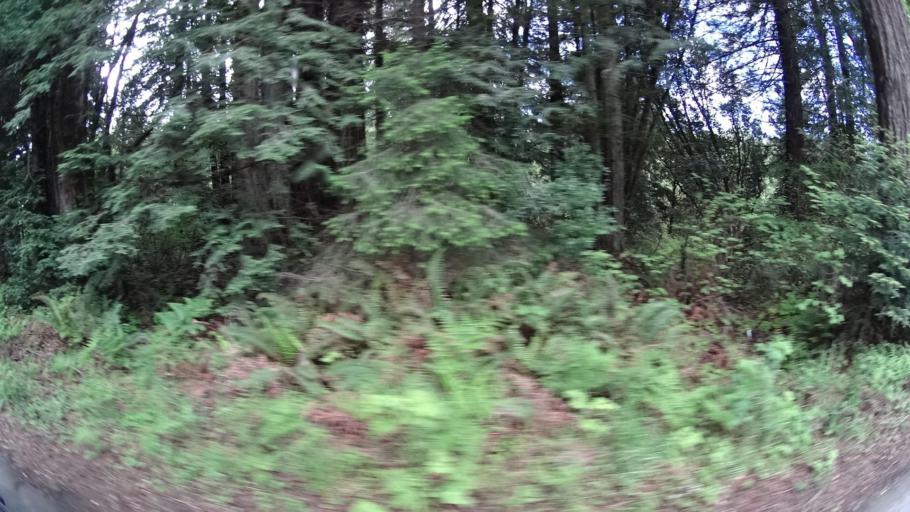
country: US
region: California
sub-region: Humboldt County
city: Blue Lake
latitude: 40.8713
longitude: -123.9748
